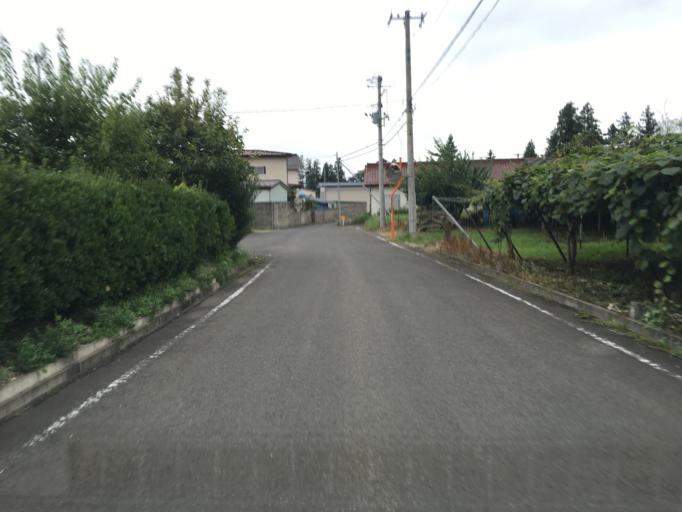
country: JP
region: Fukushima
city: Fukushima-shi
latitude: 37.7798
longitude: 140.3831
